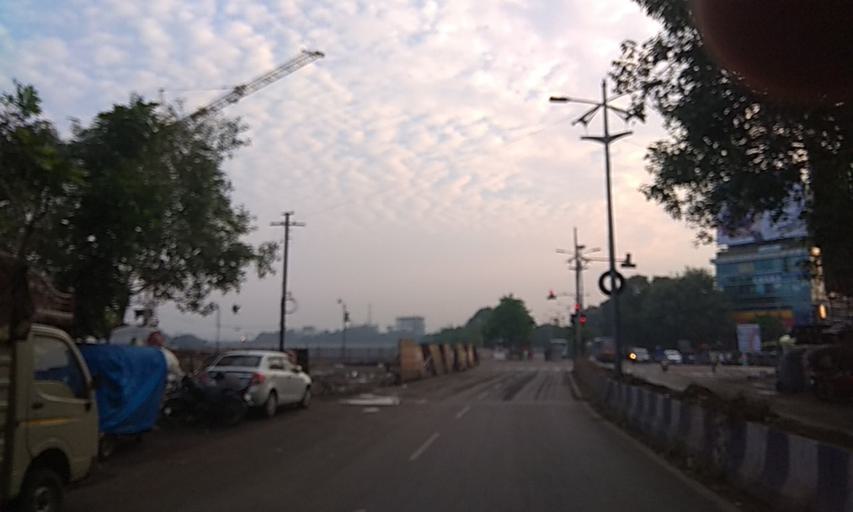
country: IN
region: Maharashtra
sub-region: Pune Division
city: Pune
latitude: 18.5237
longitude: 73.8575
